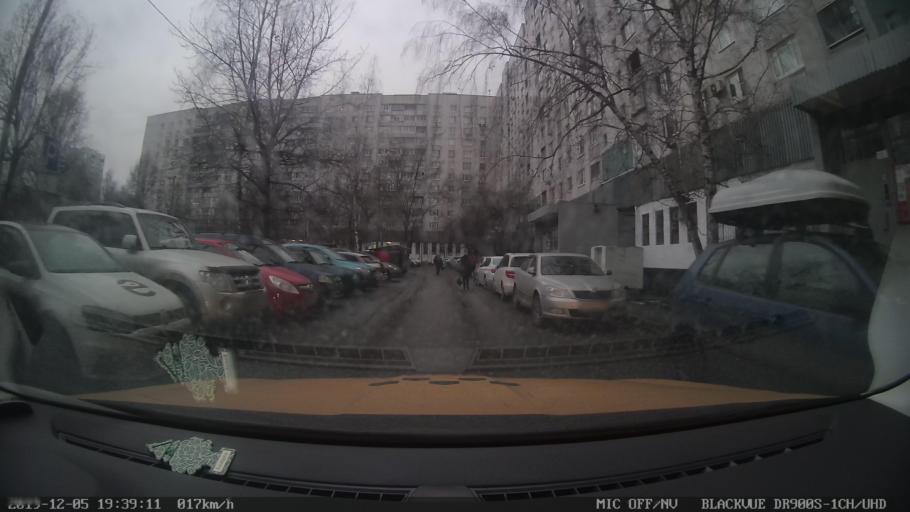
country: RU
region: Moscow
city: Lianozovo
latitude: 55.8937
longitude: 37.5917
